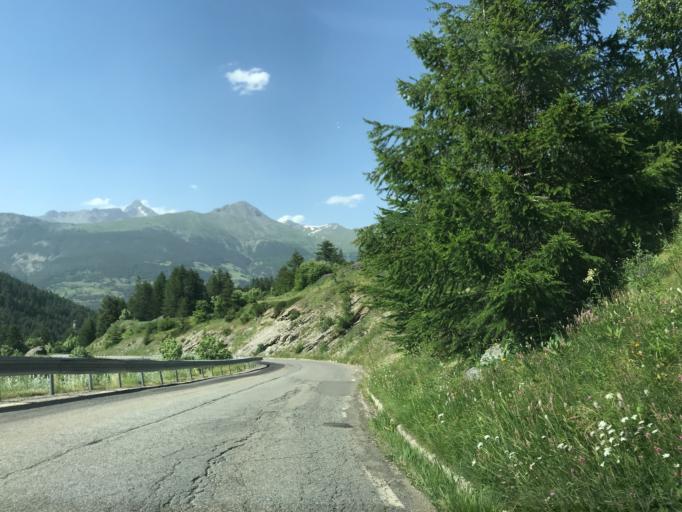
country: FR
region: Provence-Alpes-Cote d'Azur
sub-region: Departement des Hautes-Alpes
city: Guillestre
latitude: 44.7388
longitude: 6.8322
